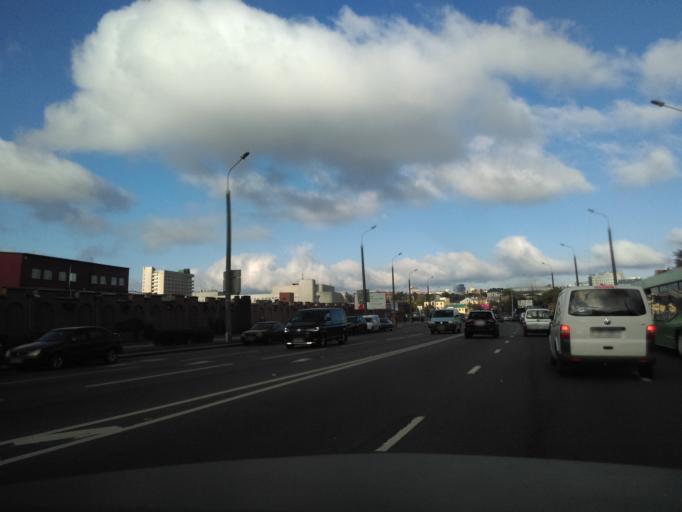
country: BY
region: Minsk
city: Minsk
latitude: 53.8929
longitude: 27.5727
